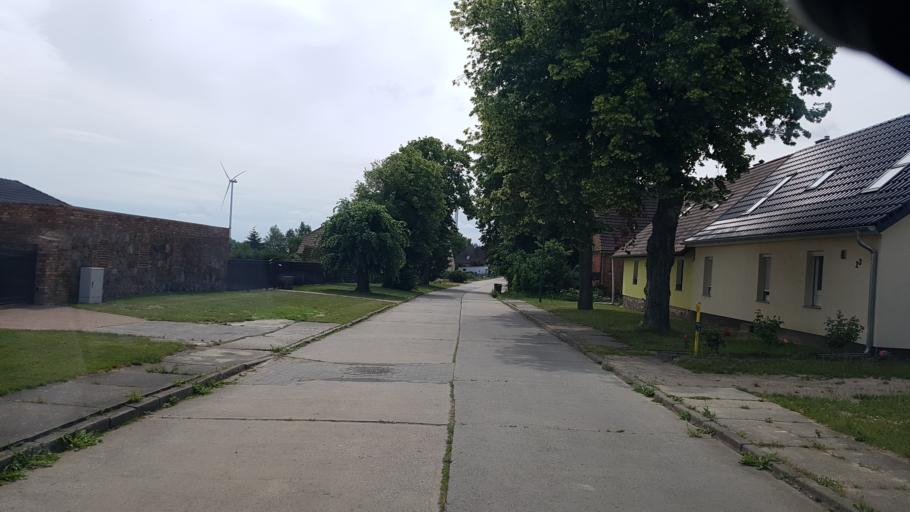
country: DE
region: Mecklenburg-Vorpommern
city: Strasburg
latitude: 53.4485
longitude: 13.8072
